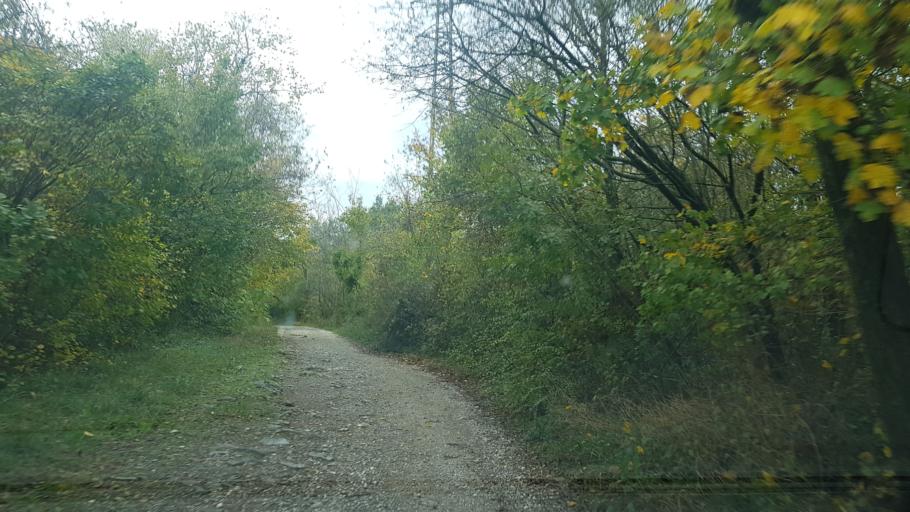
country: IT
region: Friuli Venezia Giulia
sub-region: Provincia di Gorizia
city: Monfalcone
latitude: 45.8172
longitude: 13.5324
